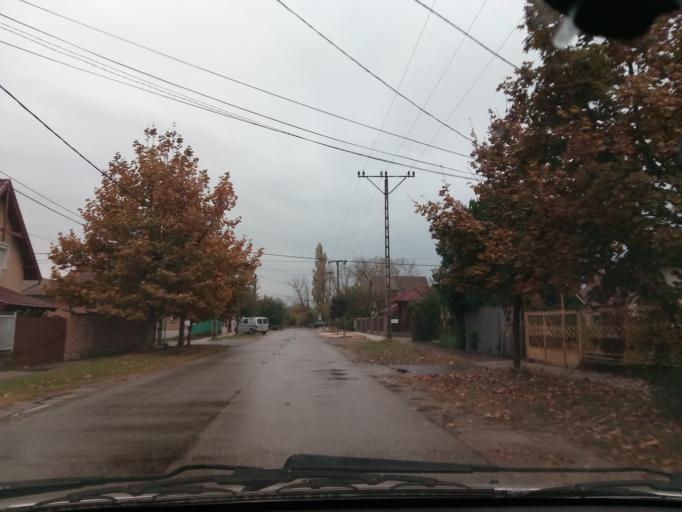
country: HU
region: Pest
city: Gyal
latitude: 47.4267
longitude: 19.2284
